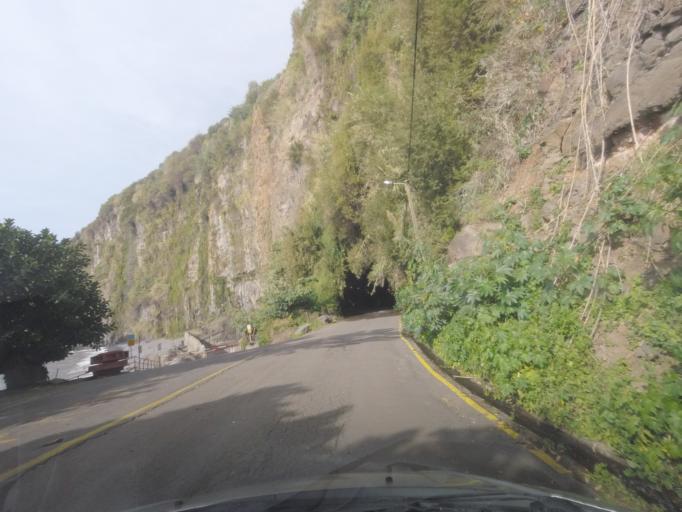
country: PT
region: Madeira
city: Ponta do Sol
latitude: 32.6906
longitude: -17.1198
